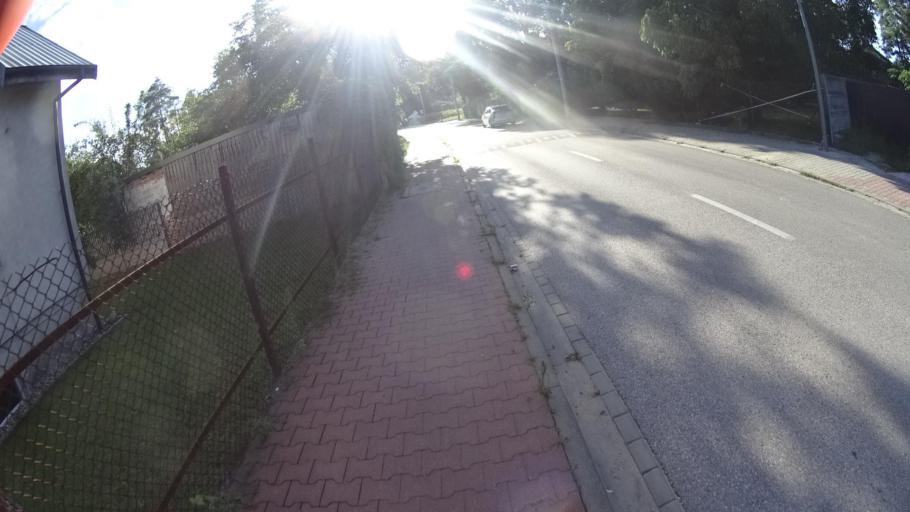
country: PL
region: Masovian Voivodeship
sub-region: Powiat piaseczynski
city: Piaseczno
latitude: 52.0644
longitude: 21.0041
